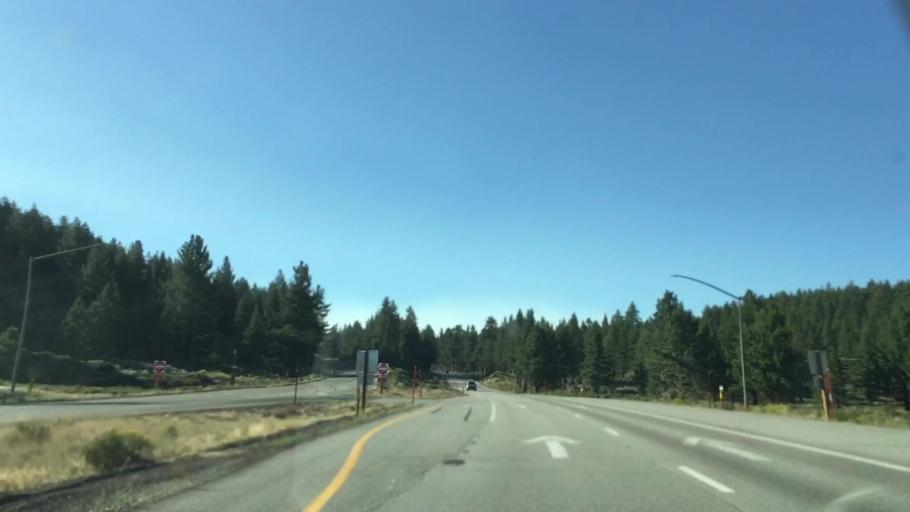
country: US
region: California
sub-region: Mono County
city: Mammoth Lakes
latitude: 37.6570
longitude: -118.9252
